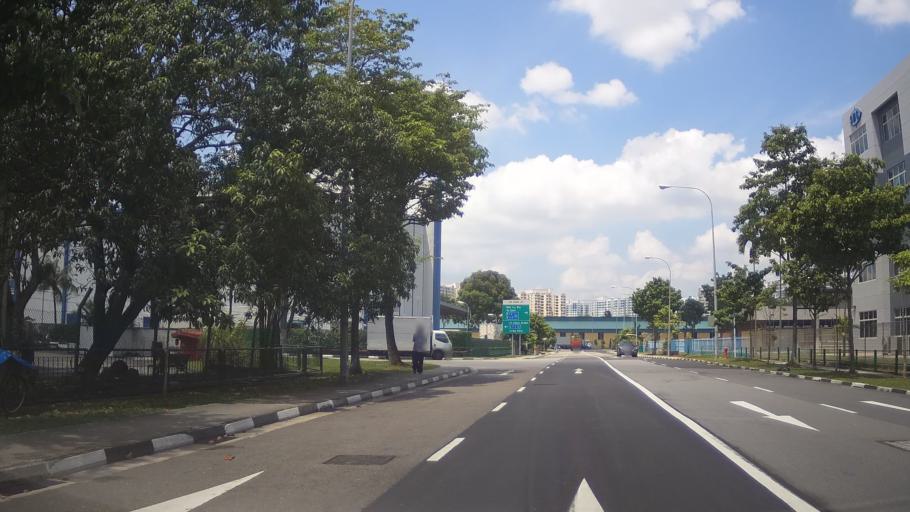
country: MY
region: Johor
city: Johor Bahru
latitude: 1.3360
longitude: 103.7114
